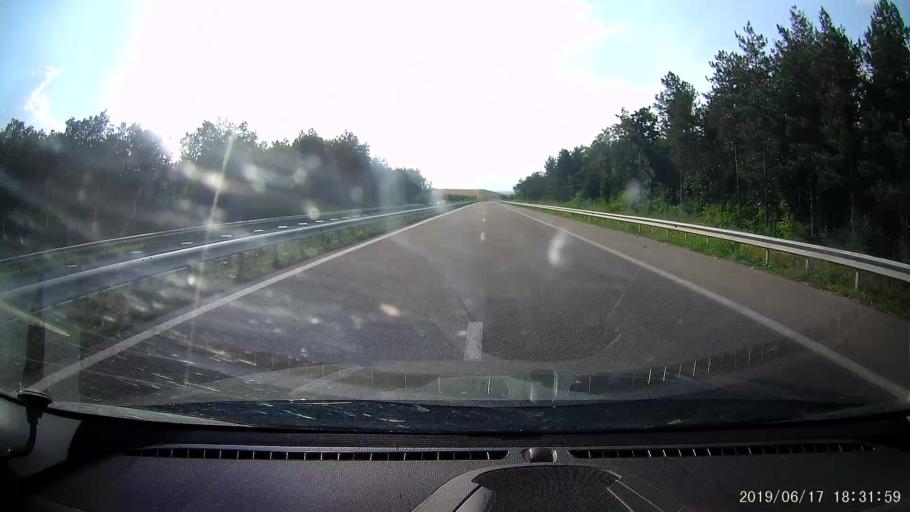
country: BG
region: Khaskovo
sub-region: Obshtina Dimitrovgrad
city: Dimitrovgrad
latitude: 42.0532
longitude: 25.4905
